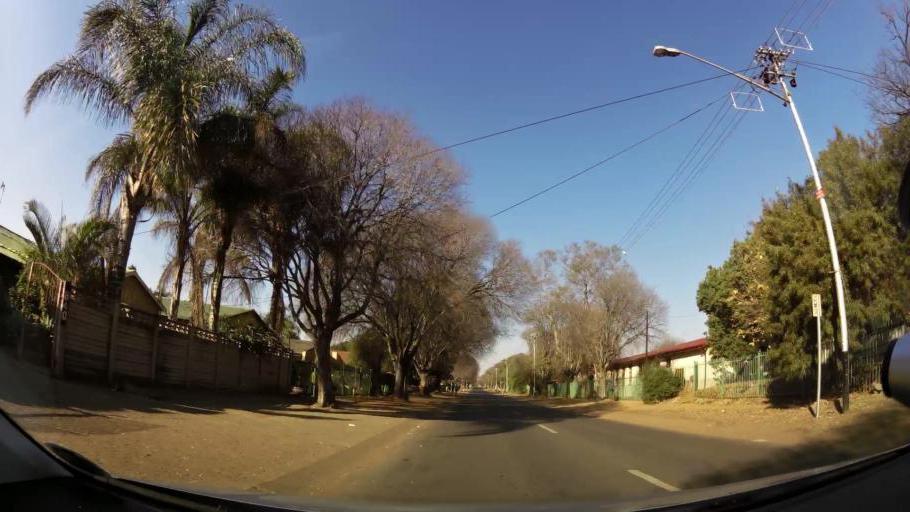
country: ZA
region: Gauteng
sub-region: City of Tshwane Metropolitan Municipality
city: Pretoria
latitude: -25.7127
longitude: 28.1420
